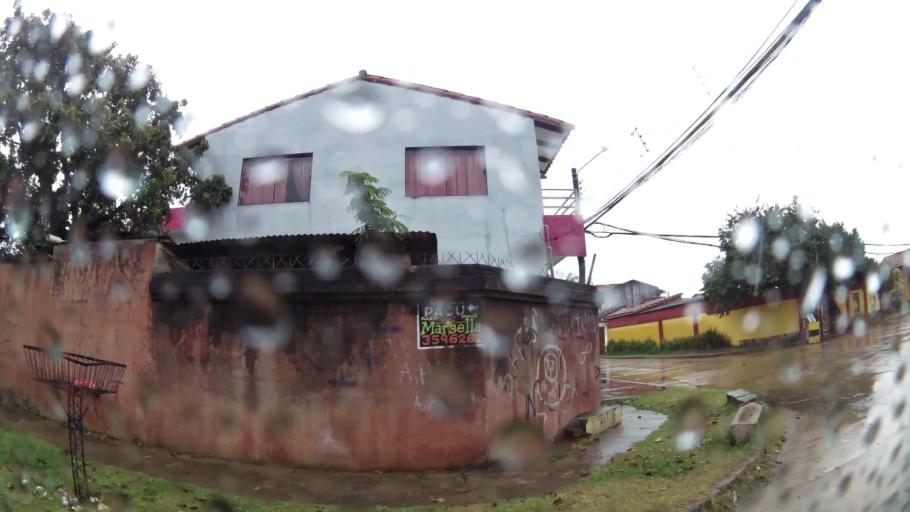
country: BO
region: Santa Cruz
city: Santa Cruz de la Sierra
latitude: -17.7941
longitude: -63.2186
